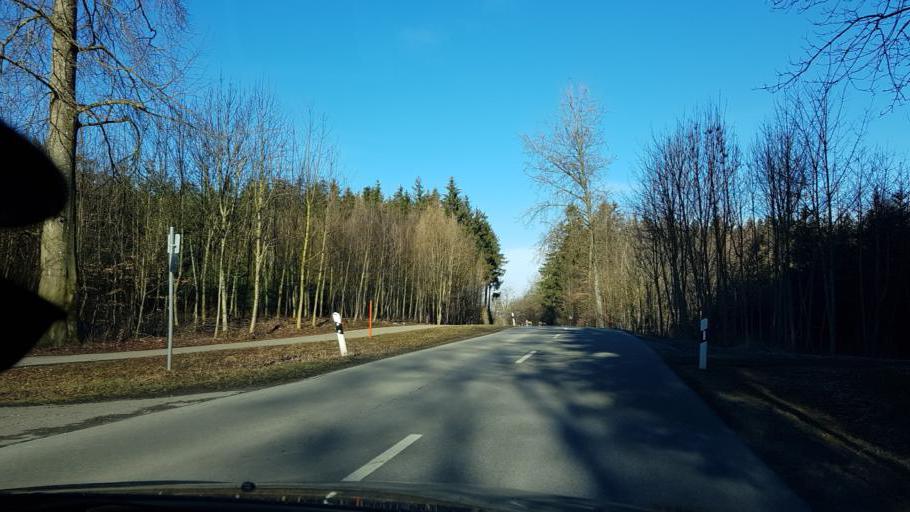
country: DE
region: Bavaria
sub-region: Upper Bavaria
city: Oberschweinbach
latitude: 48.2320
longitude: 11.1677
